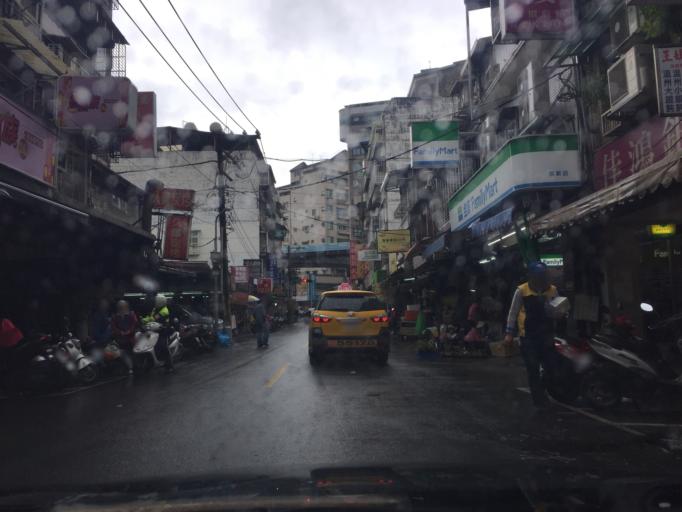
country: TW
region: Taipei
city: Taipei
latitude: 25.0804
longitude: 121.5918
